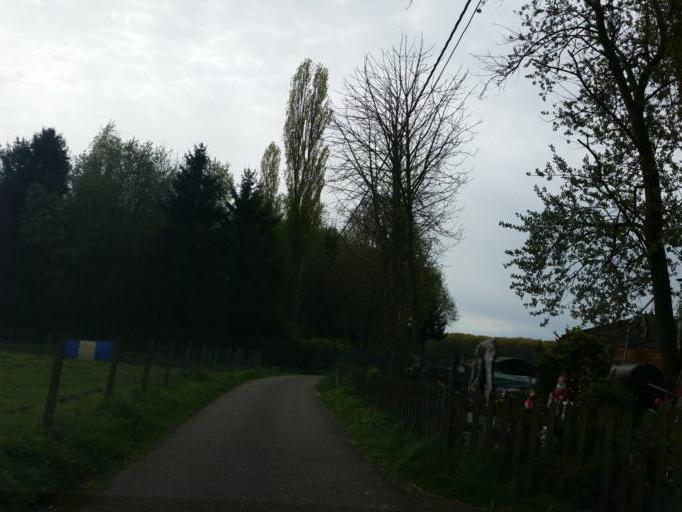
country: BE
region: Flanders
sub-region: Provincie Vlaams-Brabant
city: Kampenhout
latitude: 50.9736
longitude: 4.5338
